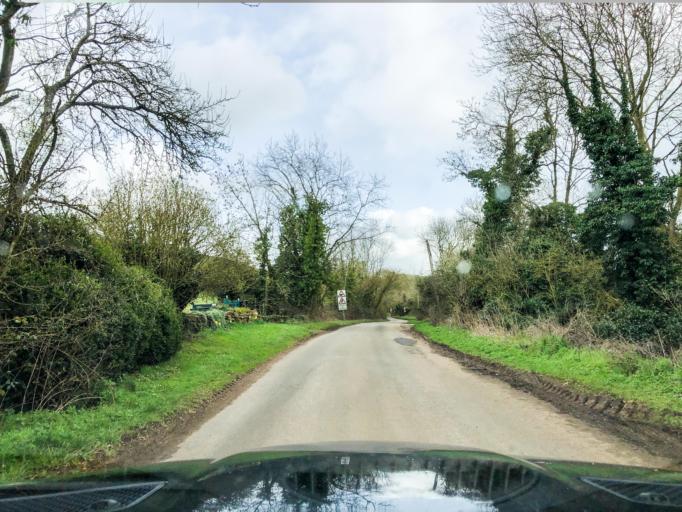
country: GB
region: England
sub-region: Warwickshire
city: Harbury
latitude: 52.1647
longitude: -1.4308
